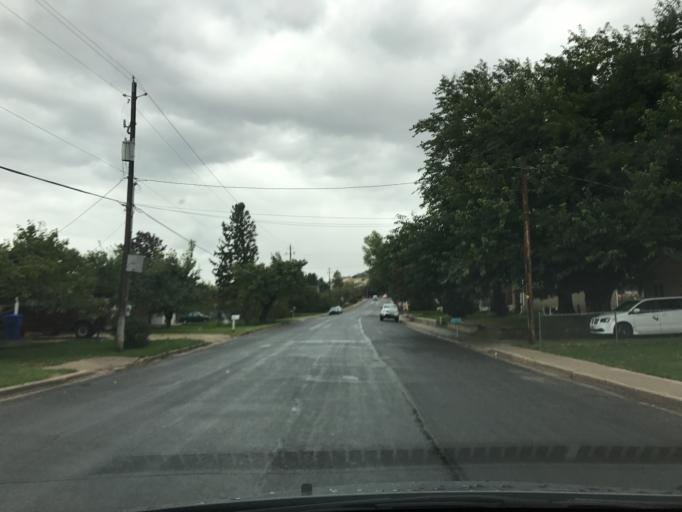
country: US
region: Utah
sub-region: Davis County
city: Farmington
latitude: 40.9955
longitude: -111.8941
